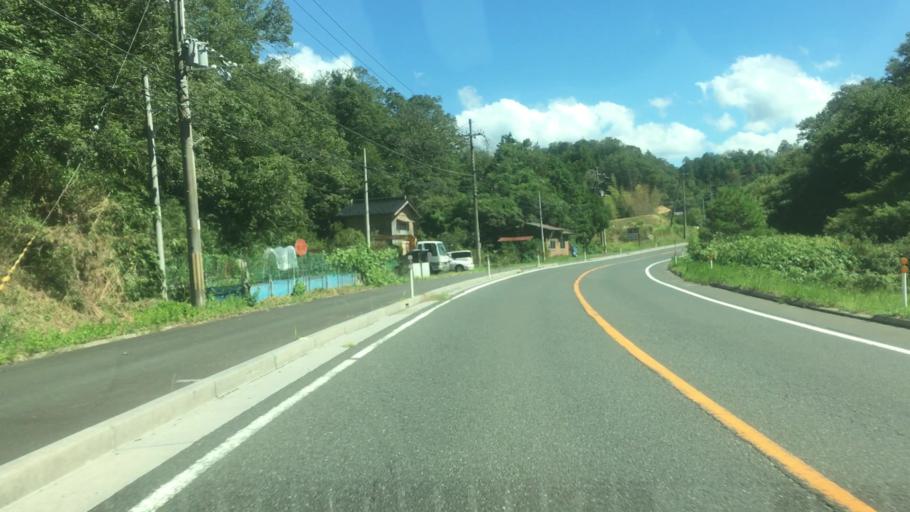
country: JP
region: Hyogo
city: Toyooka
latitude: 35.5860
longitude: 134.9521
